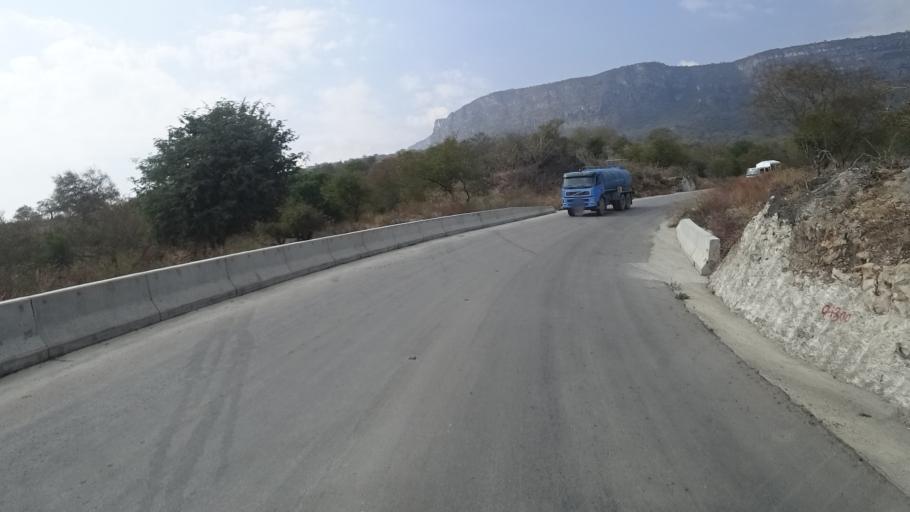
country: YE
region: Al Mahrah
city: Hawf
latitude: 16.7109
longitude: 53.2523
